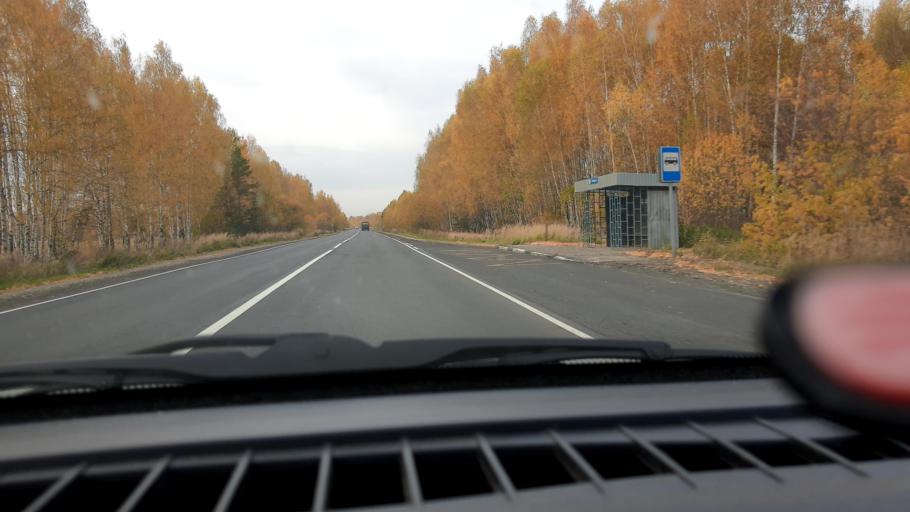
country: RU
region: Nizjnij Novgorod
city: Novaya Balakhna
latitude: 56.5696
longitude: 43.7124
